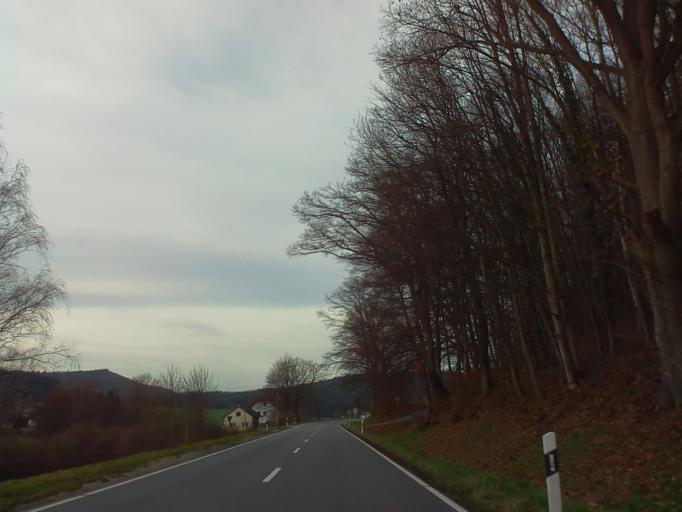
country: DE
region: Hesse
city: Reichelsheim
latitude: 49.6414
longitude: 8.8971
